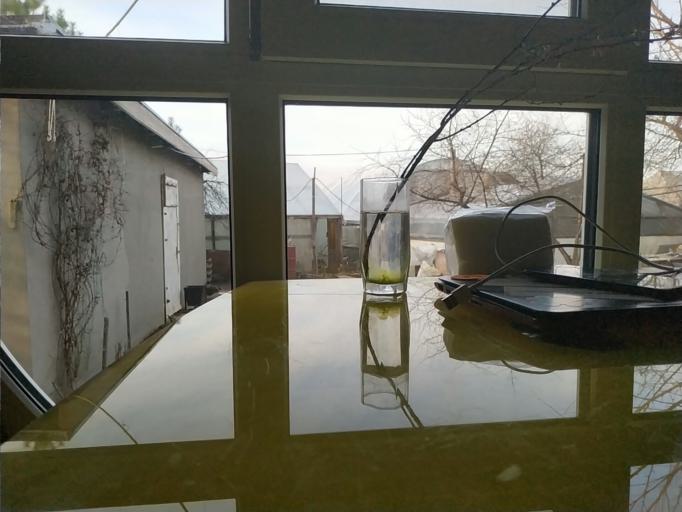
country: RU
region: Republic of Karelia
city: Suoyarvi
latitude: 62.0689
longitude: 32.1781
